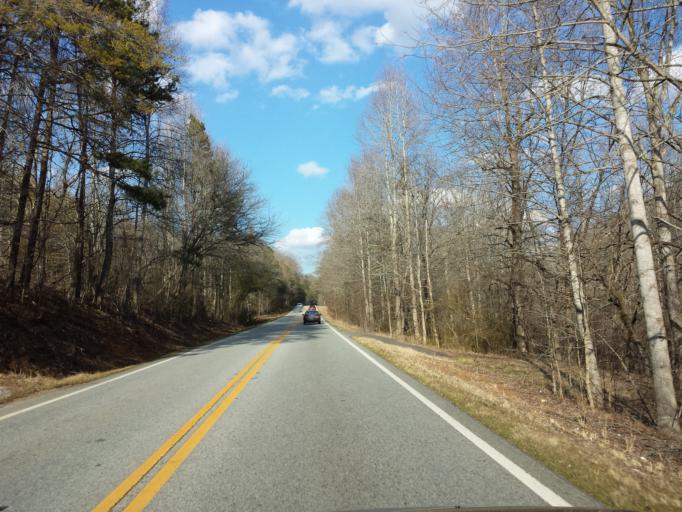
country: US
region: Georgia
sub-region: Lumpkin County
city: Dahlonega
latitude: 34.5114
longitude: -83.9246
